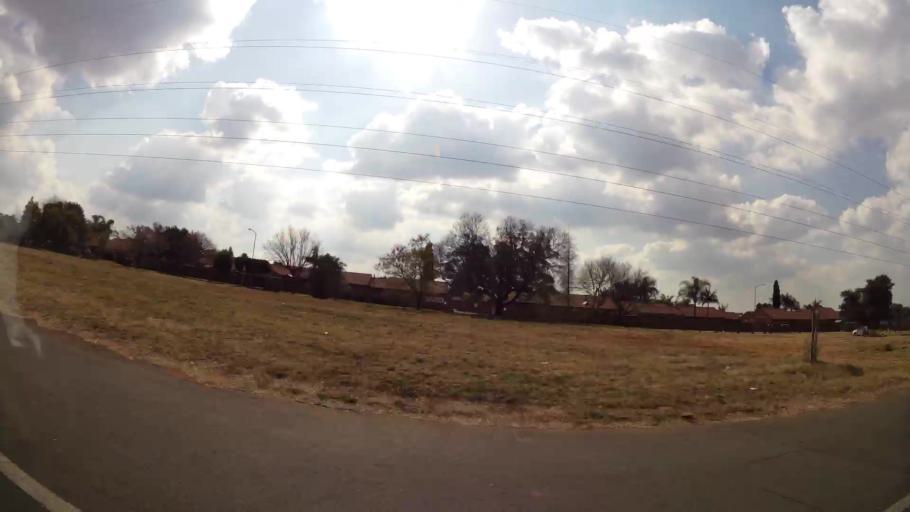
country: ZA
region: Gauteng
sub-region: City of Tshwane Metropolitan Municipality
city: Centurion
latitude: -25.8231
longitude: 28.2572
